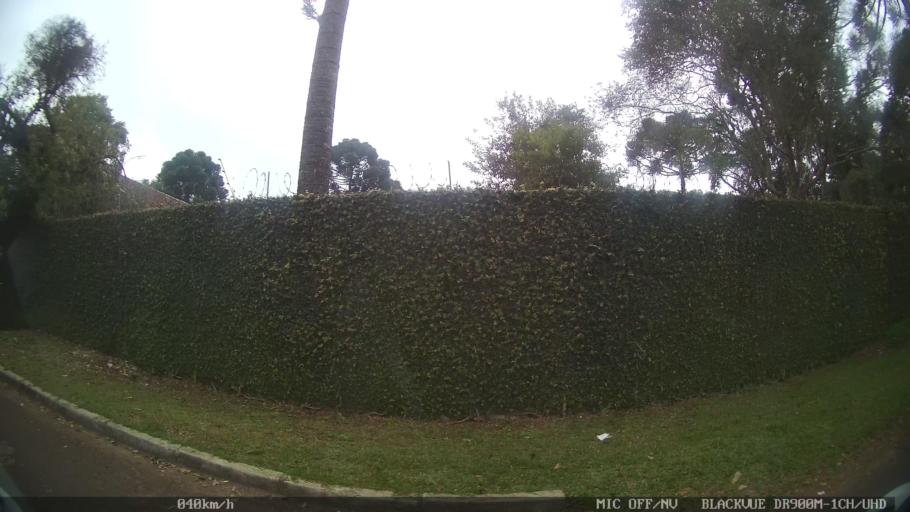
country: BR
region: Parana
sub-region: Curitiba
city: Curitiba
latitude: -25.3955
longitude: -49.3193
